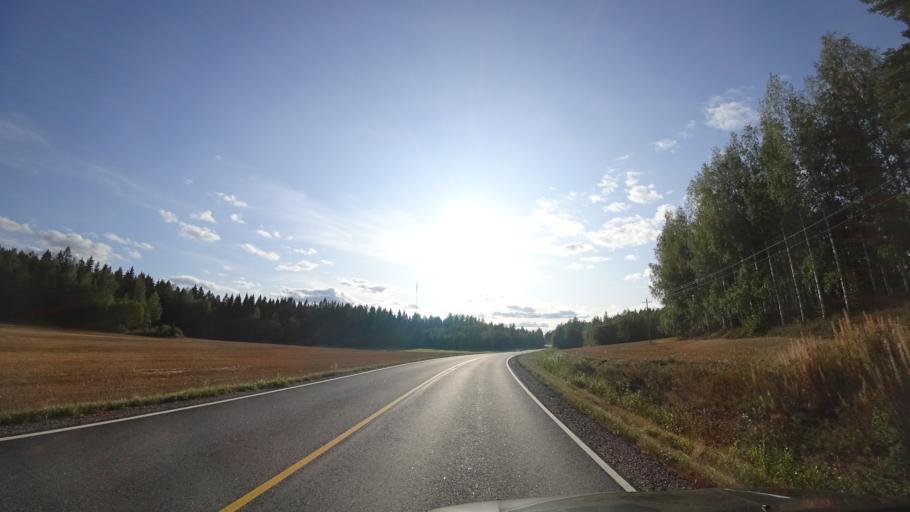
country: FI
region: Paijanne Tavastia
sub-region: Lahti
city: Hollola
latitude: 61.1440
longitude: 25.3474
